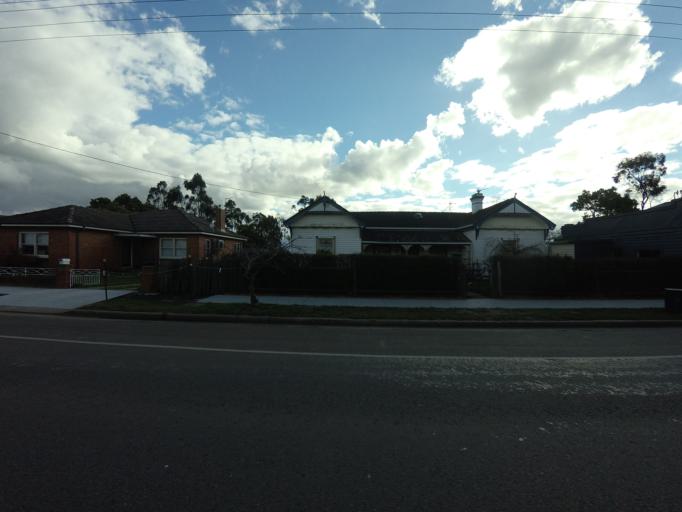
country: AU
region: Tasmania
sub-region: Northern Midlands
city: Longford
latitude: -41.6859
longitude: 147.0803
